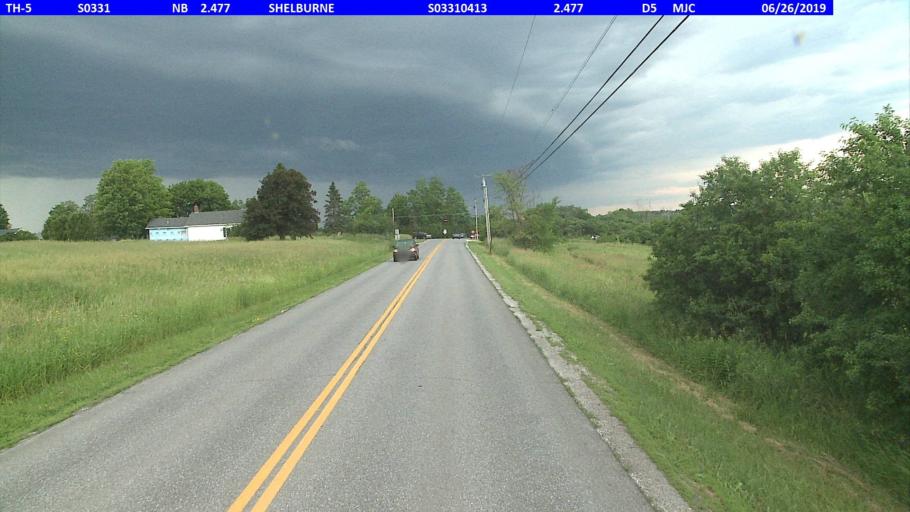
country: US
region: Vermont
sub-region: Chittenden County
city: South Burlington
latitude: 44.4060
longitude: -73.1780
